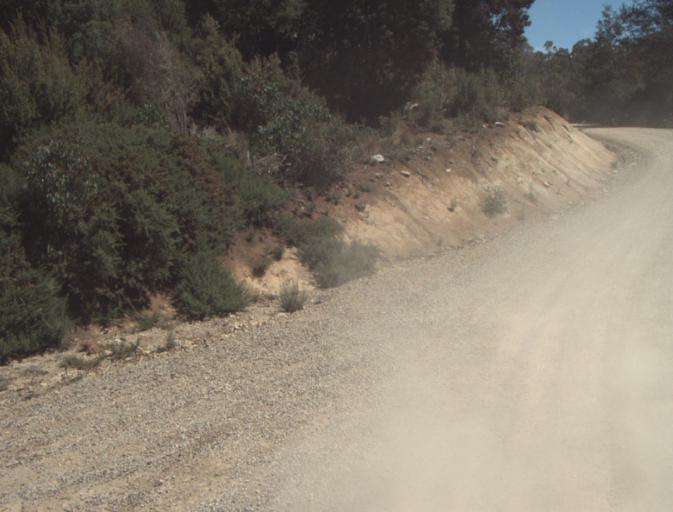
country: AU
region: Tasmania
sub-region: Dorset
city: Scottsdale
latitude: -41.3172
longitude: 147.4647
